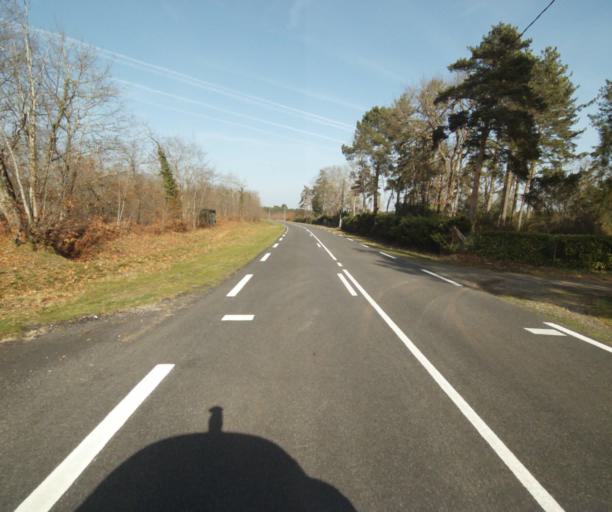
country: FR
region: Aquitaine
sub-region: Departement de la Gironde
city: Grignols
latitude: 44.2048
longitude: -0.1512
